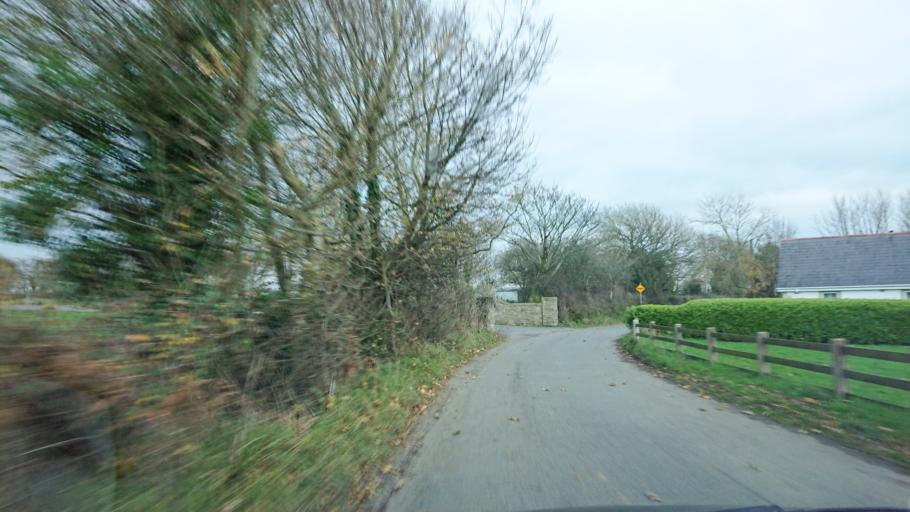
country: IE
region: Munster
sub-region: Waterford
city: Dunmore East
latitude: 52.2456
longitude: -6.9980
